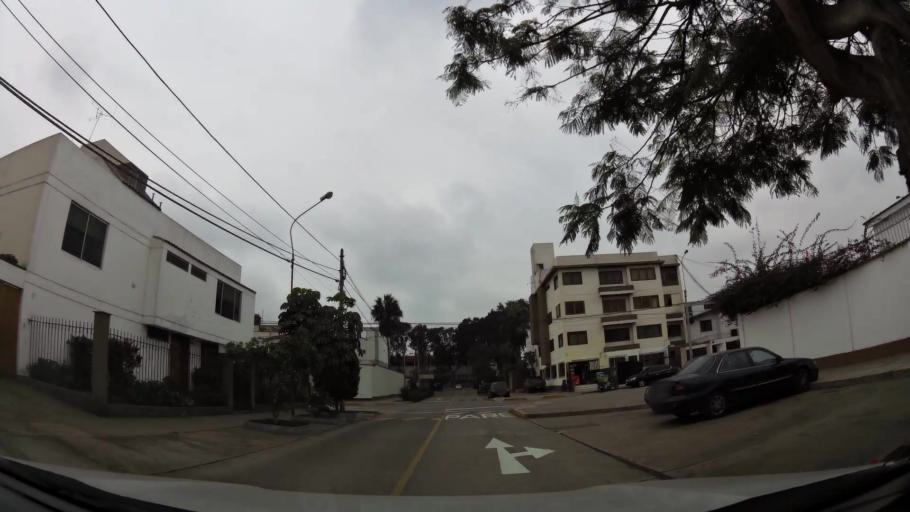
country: PE
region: Lima
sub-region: Lima
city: San Luis
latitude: -12.0991
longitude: -76.9968
